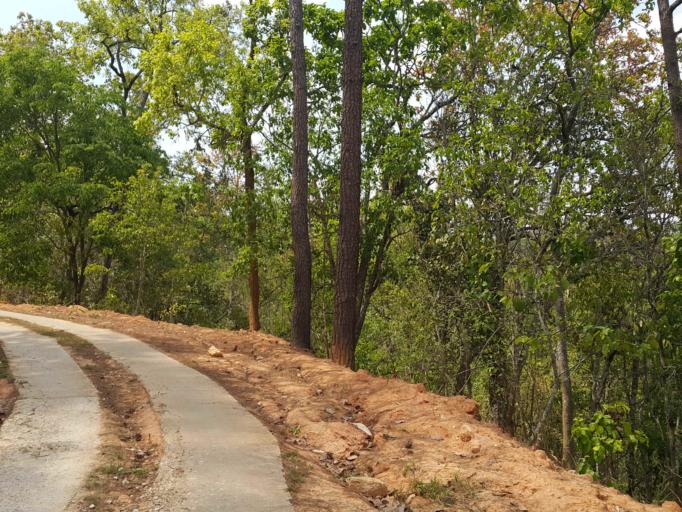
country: TH
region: Chiang Mai
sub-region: Amphoe Chiang Dao
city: Chiang Dao
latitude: 19.3042
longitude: 98.7405
